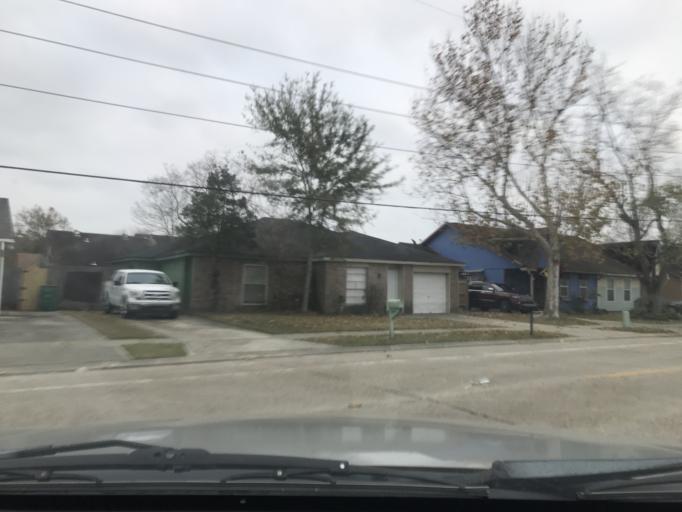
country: US
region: Louisiana
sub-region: Jefferson Parish
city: Woodmere
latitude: 29.8602
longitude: -90.0745
